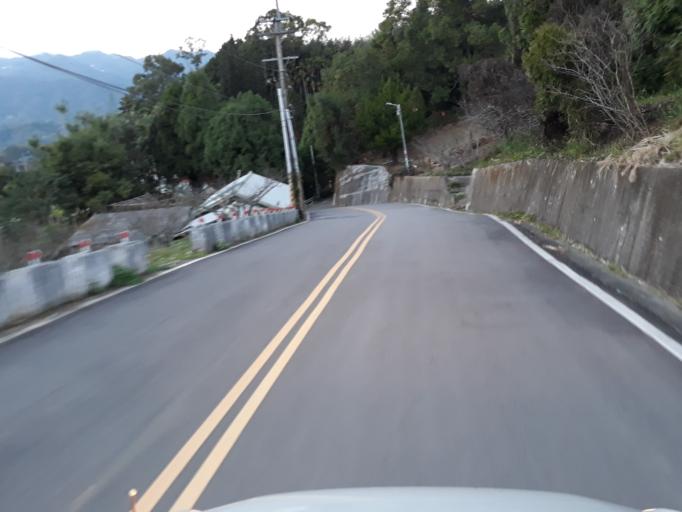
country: TW
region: Taiwan
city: Fengyuan
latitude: 24.3579
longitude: 120.8676
